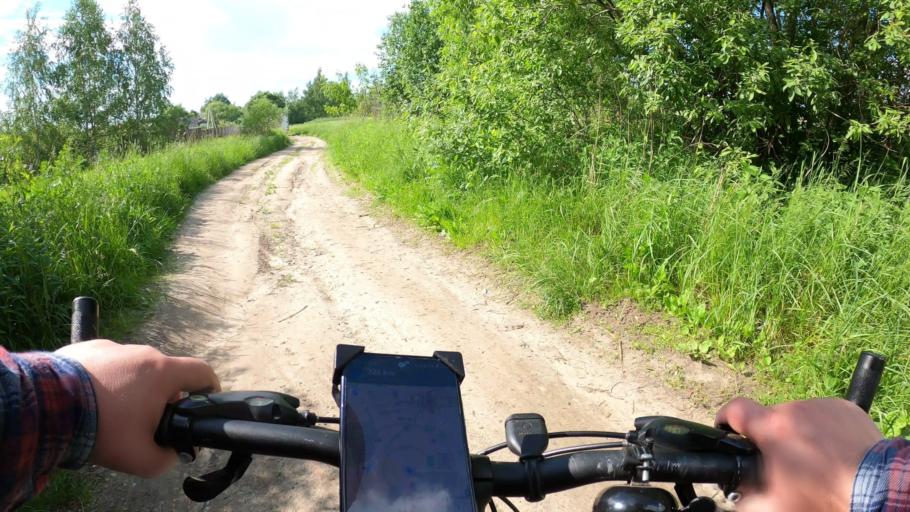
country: RU
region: Moskovskaya
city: Konobeyevo
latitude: 55.4156
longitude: 38.6559
